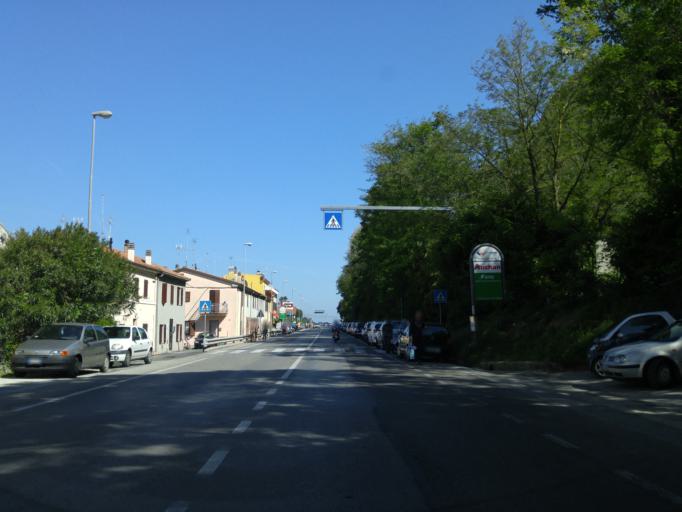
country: IT
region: The Marches
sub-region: Provincia di Pesaro e Urbino
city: Pesaro
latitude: 43.9020
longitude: 12.9332
